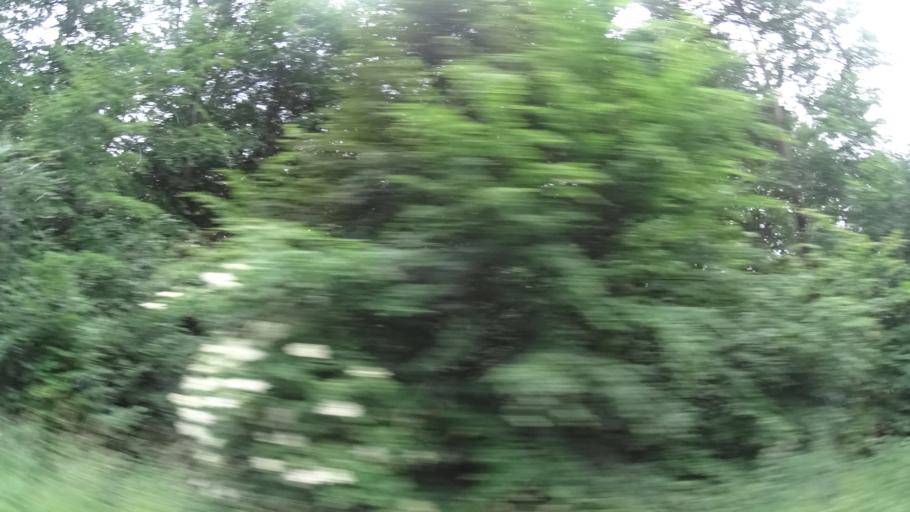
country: DE
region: Lower Saxony
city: Vahlbruch
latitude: 51.8909
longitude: 9.3175
